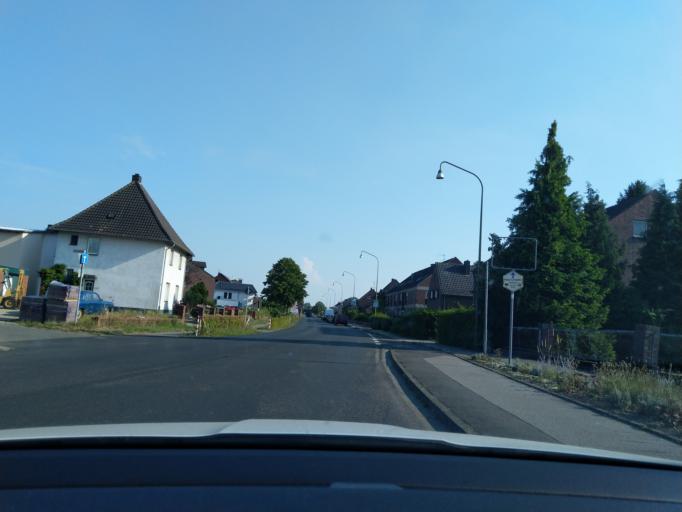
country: DE
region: North Rhine-Westphalia
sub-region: Regierungsbezirk Koln
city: Wassenberg
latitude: 51.1290
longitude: 6.1910
